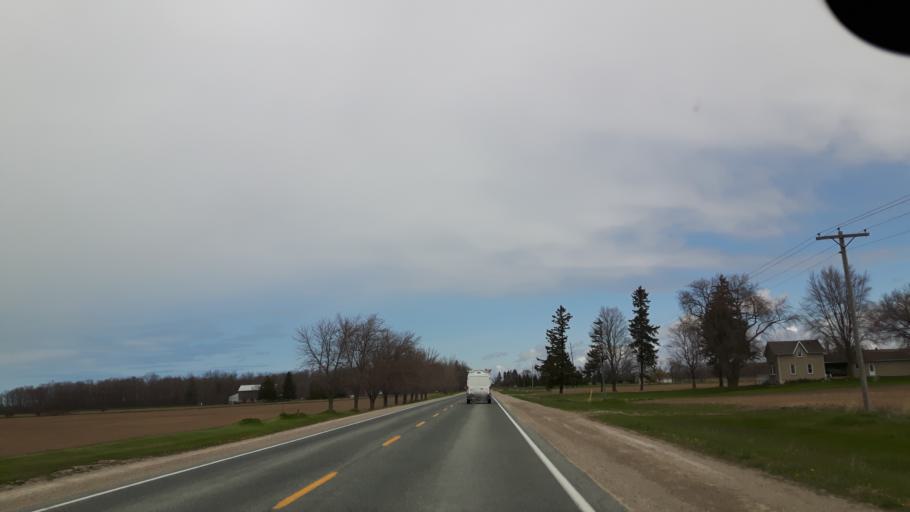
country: CA
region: Ontario
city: Bluewater
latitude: 43.4961
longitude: -81.6960
